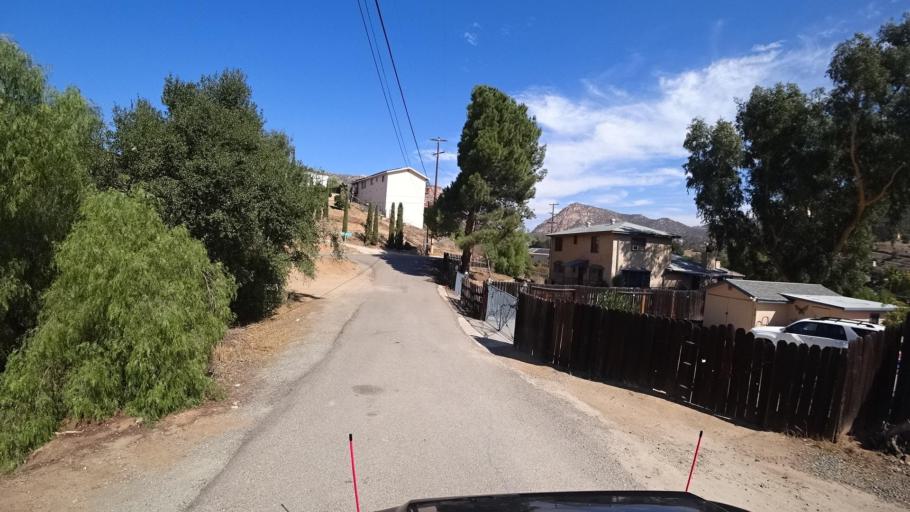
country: US
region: California
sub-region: San Diego County
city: Harbison Canyon
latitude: 32.8156
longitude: -116.8368
